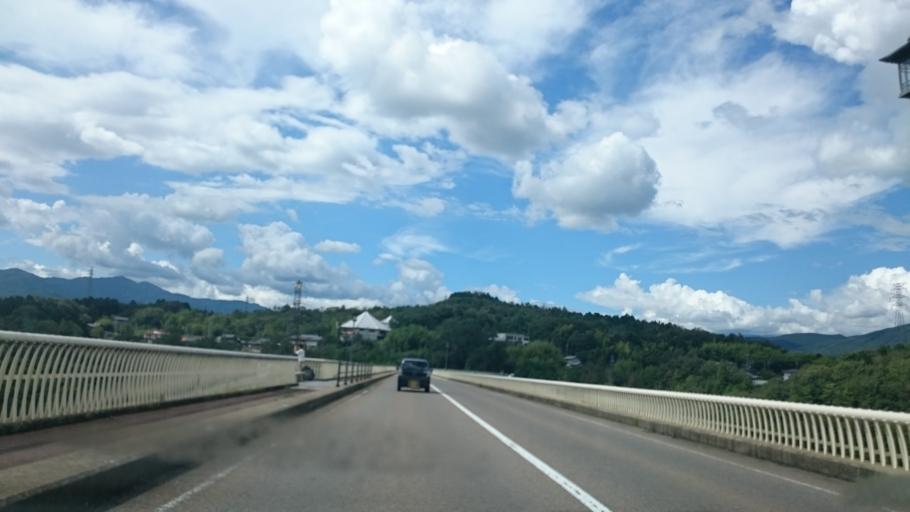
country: JP
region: Gifu
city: Nakatsugawa
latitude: 35.5085
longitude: 137.4748
